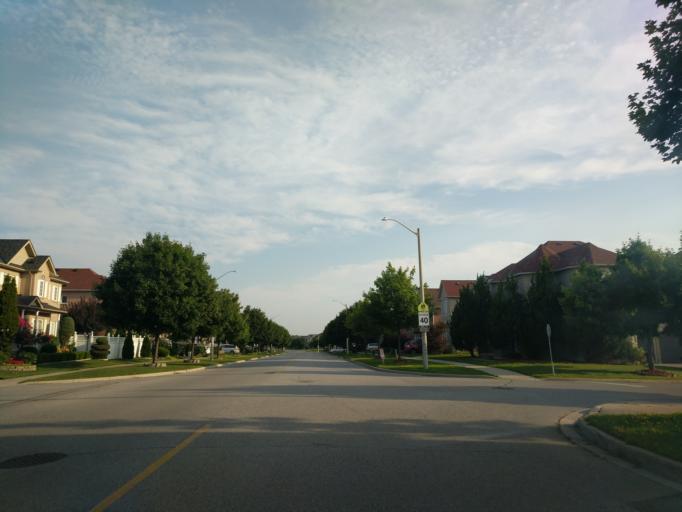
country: CA
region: Ontario
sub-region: York
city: Richmond Hill
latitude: 43.8798
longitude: -79.4010
